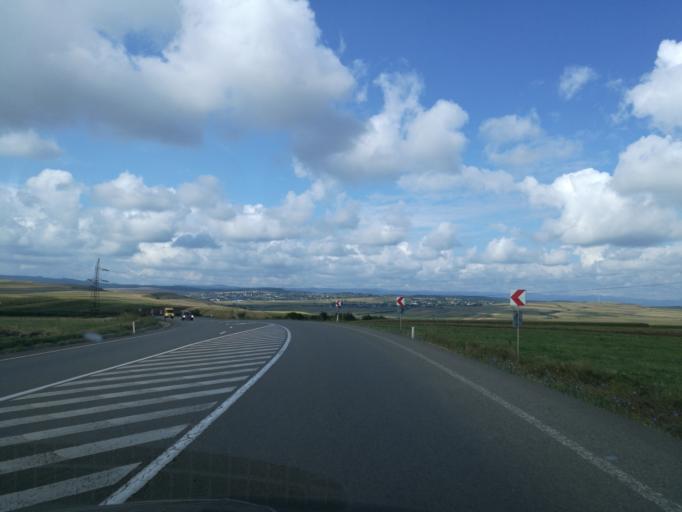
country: RO
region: Suceava
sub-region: Comuna Stroesti
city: Stroesti
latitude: 47.6238
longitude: 26.1033
